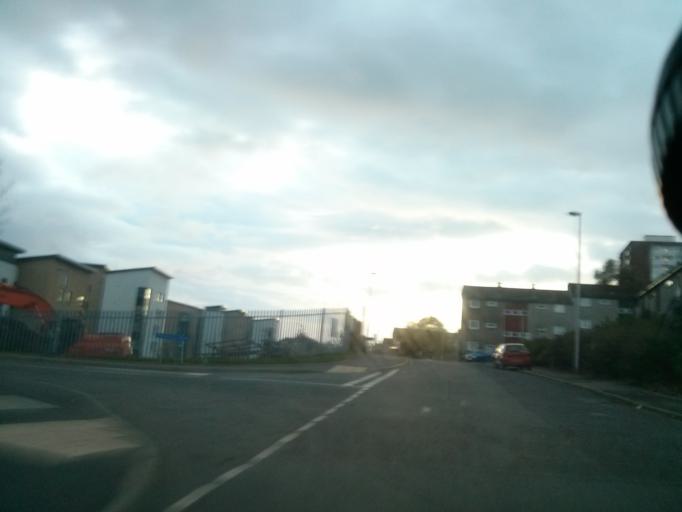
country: GB
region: Scotland
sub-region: Aberdeen City
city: Aberdeen
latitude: 57.1739
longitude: -2.1150
